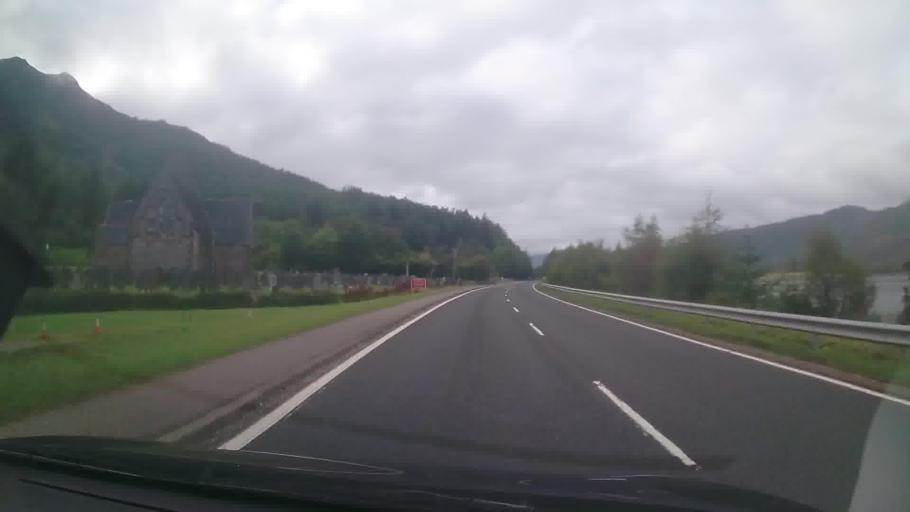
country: GB
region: Scotland
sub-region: Highland
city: Fort William
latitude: 56.6772
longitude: -5.1544
